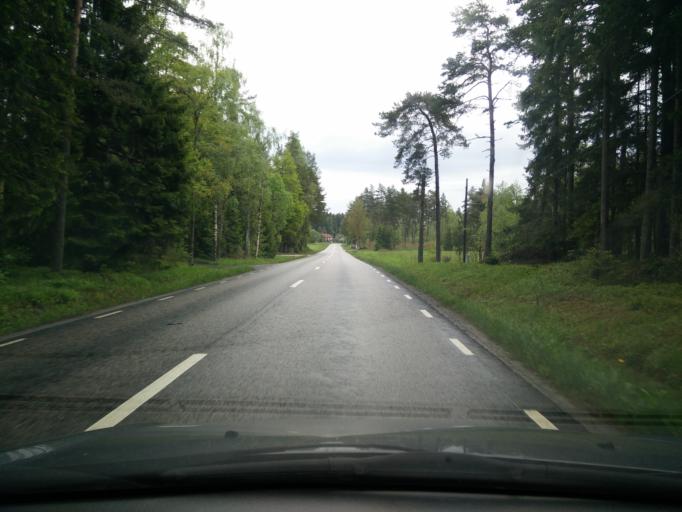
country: SE
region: Stockholm
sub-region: Norrtalje Kommun
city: Bjorko
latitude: 59.7926
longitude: 18.8673
